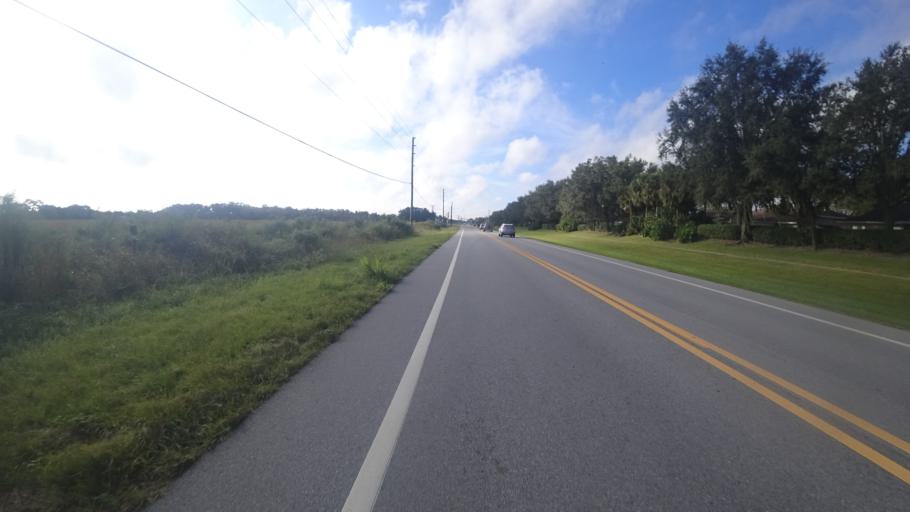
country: US
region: Florida
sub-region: Manatee County
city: Ellenton
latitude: 27.5512
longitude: -82.4254
